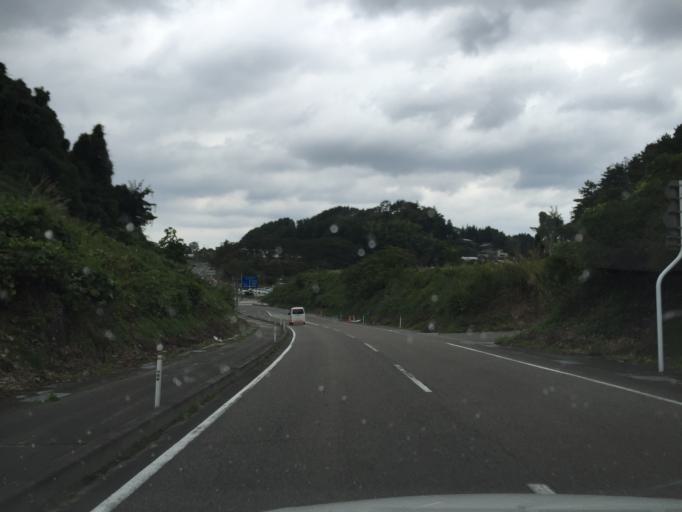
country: JP
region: Fukushima
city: Miharu
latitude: 37.4418
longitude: 140.5107
